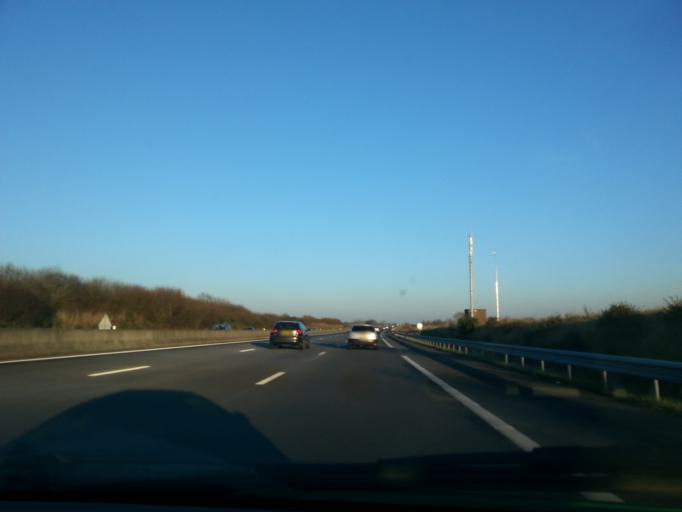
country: FR
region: Pays de la Loire
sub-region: Departement de la Sarthe
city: Tuffe
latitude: 48.1063
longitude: 0.5514
